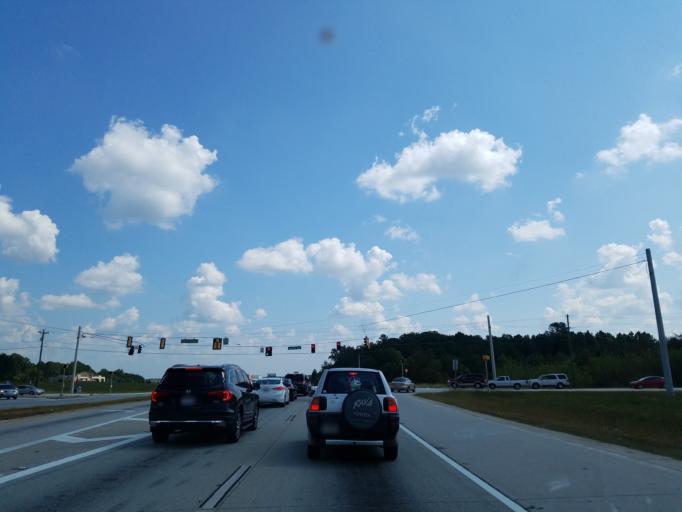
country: US
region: Georgia
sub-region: Barrow County
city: Winder
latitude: 33.9464
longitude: -83.7550
